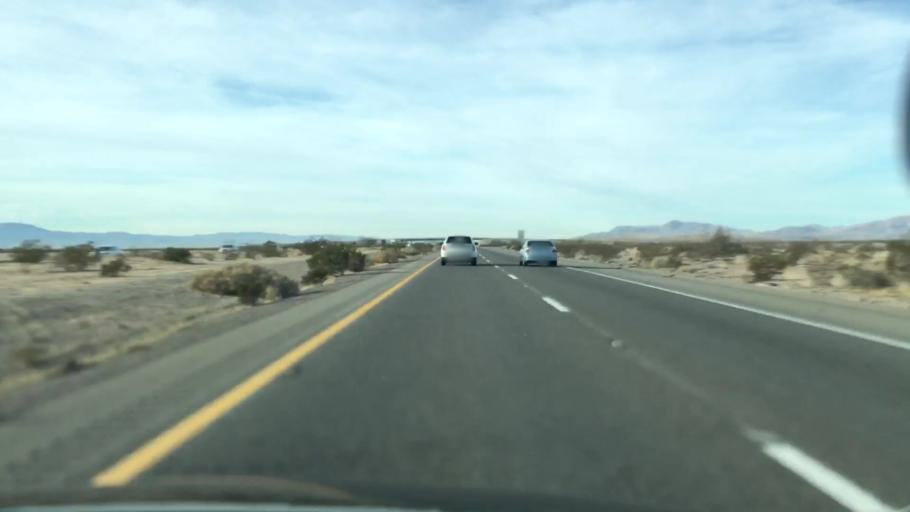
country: US
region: California
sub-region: San Bernardino County
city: Fort Irwin
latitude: 34.9881
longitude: -116.5894
